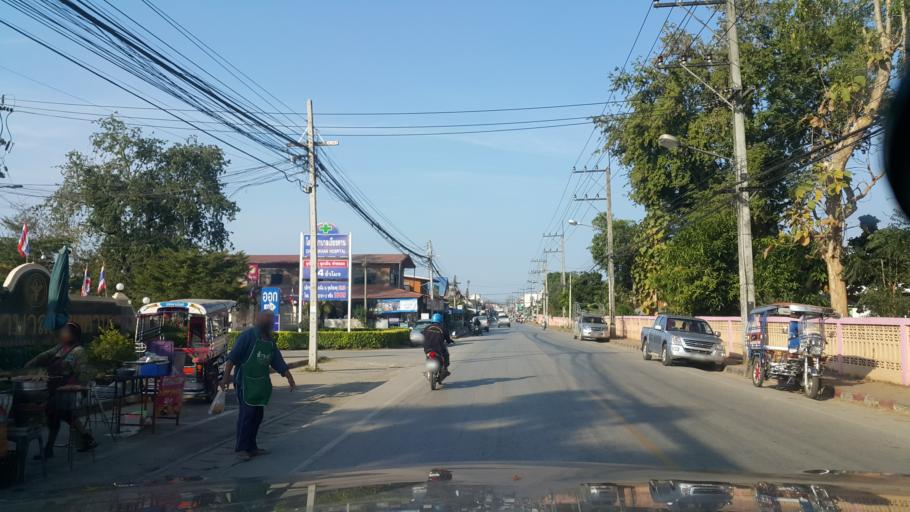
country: TH
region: Loei
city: Chiang Khan
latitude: 17.8939
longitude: 101.6549
